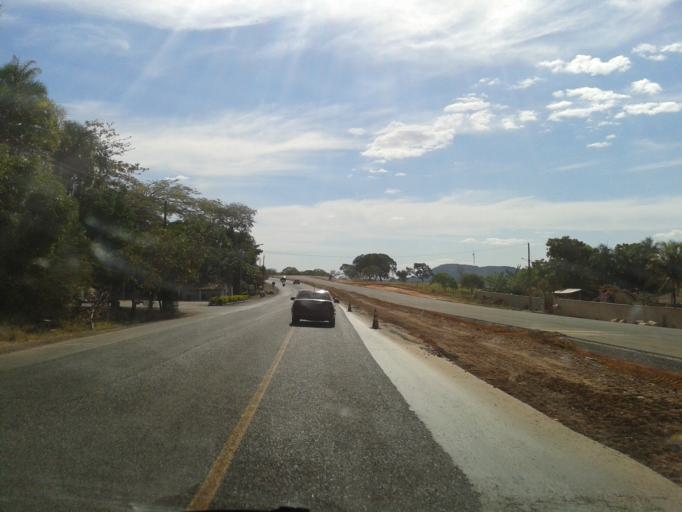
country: BR
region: Goias
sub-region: Goias
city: Goias
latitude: -15.9850
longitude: -50.0795
